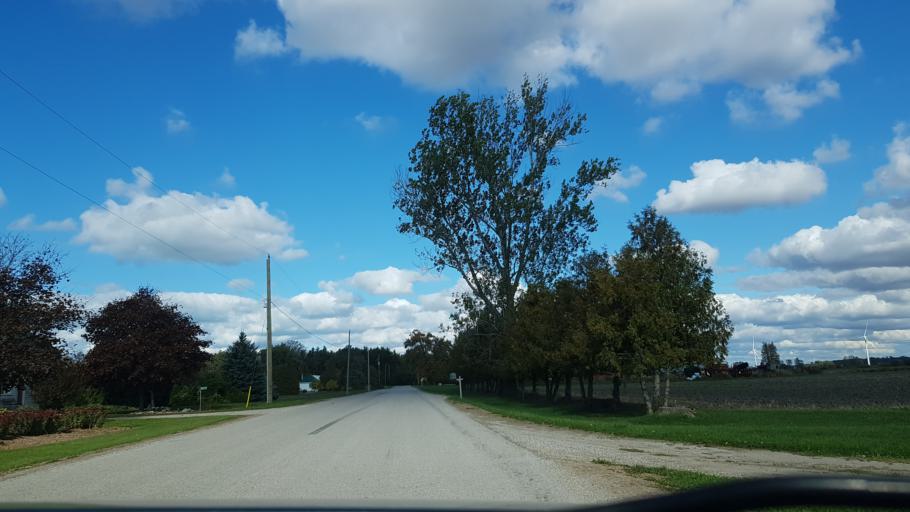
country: CA
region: Ontario
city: Lambton Shores
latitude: 43.2323
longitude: -81.7918
